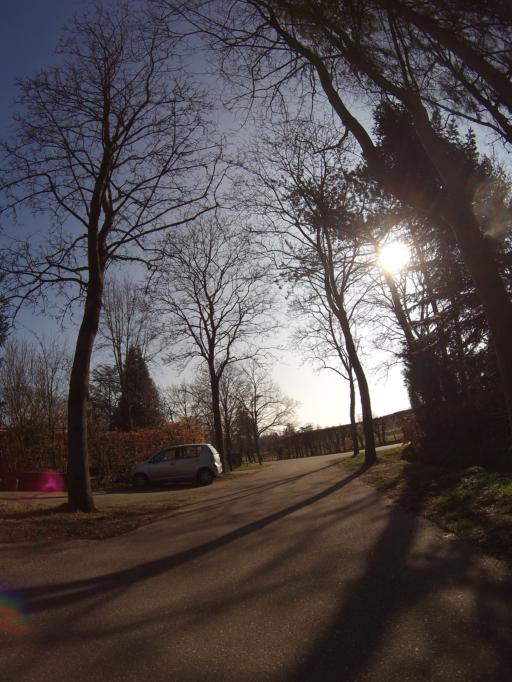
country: NL
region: Utrecht
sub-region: Gemeente Amersfoort
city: Randenbroek
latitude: 52.1220
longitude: 5.3992
